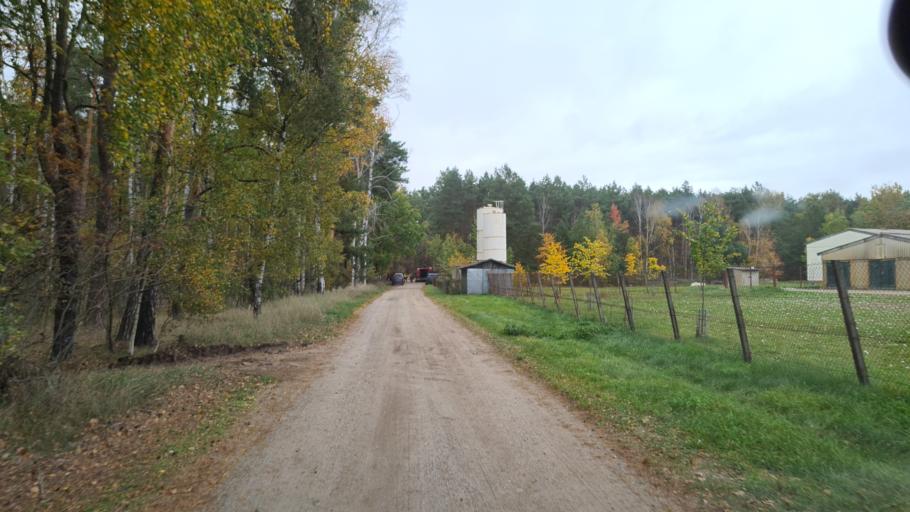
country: DE
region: Brandenburg
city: Finsterwalde
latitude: 51.6536
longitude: 13.7618
